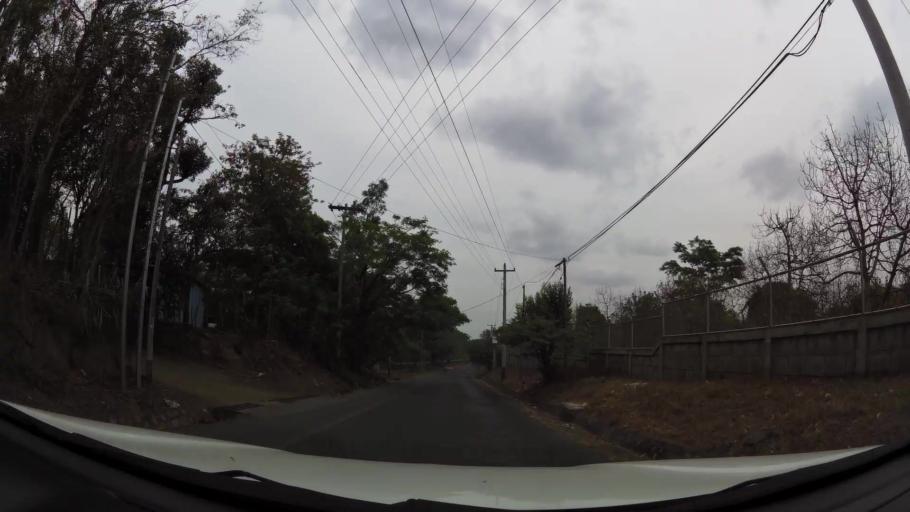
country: NI
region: Masaya
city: Ticuantepe
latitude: 12.0742
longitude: -86.1793
